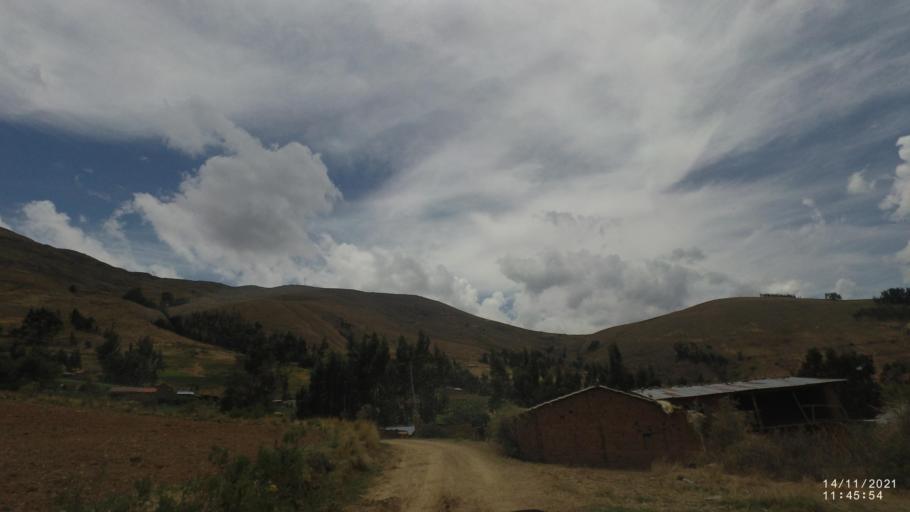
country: BO
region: Cochabamba
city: Colomi
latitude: -17.3532
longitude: -65.9881
